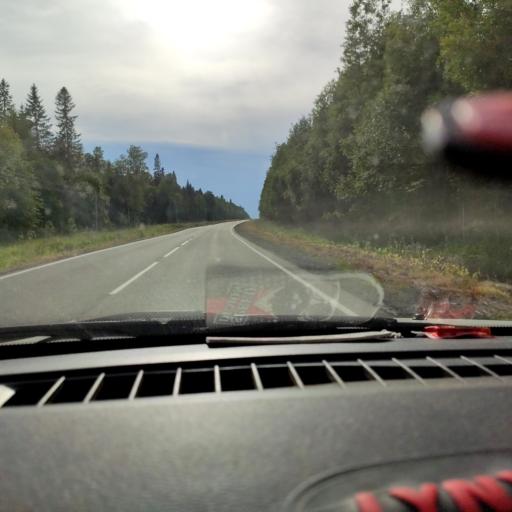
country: RU
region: Perm
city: Perm
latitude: 58.1943
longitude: 56.2411
